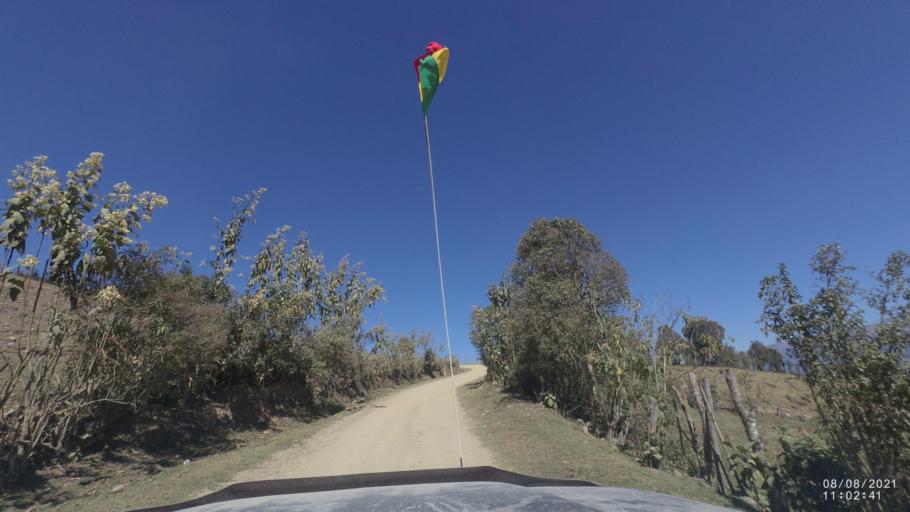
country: BO
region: Cochabamba
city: Colchani
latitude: -16.7543
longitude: -66.6882
